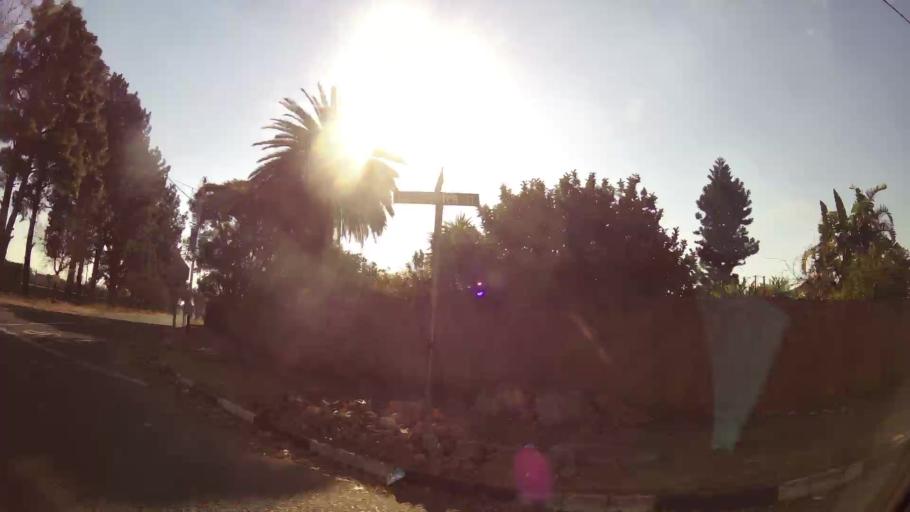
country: ZA
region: Gauteng
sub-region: City of Johannesburg Metropolitan Municipality
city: Johannesburg
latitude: -26.2484
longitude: 28.0116
